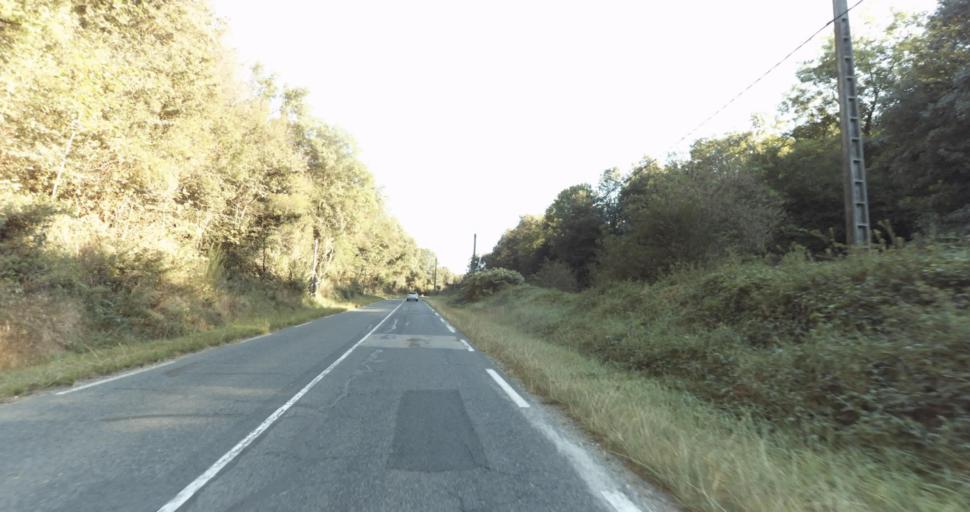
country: FR
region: Rhone-Alpes
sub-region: Departement du Rhone
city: Montanay
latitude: 45.8918
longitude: 4.8605
